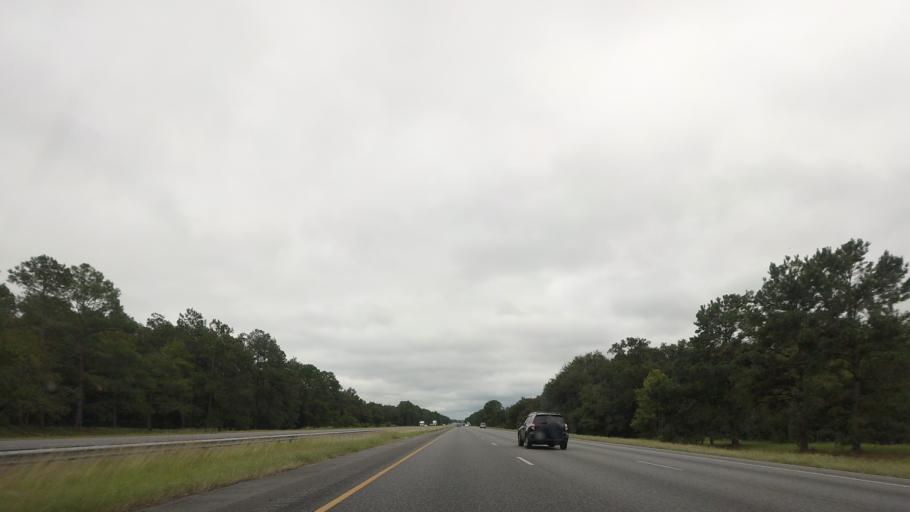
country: US
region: Georgia
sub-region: Lowndes County
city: Valdosta
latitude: 30.7214
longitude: -83.2570
